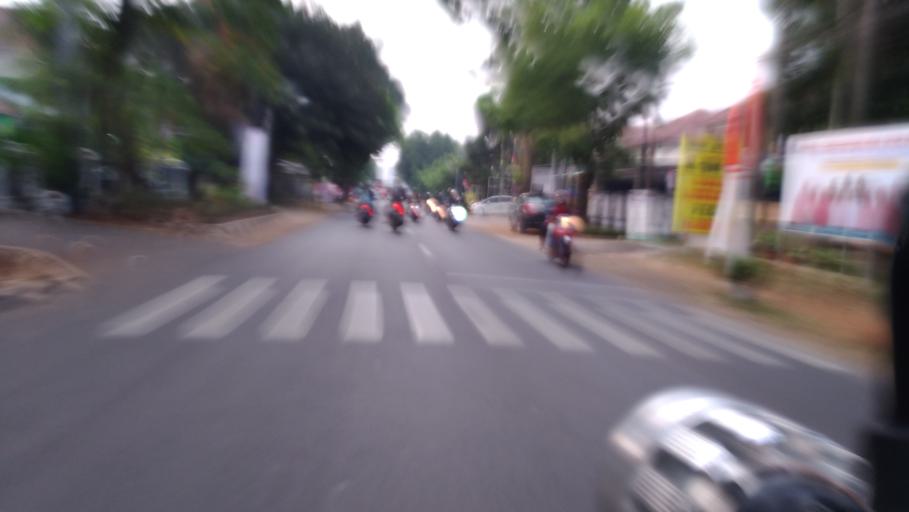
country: ID
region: West Java
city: Cileungsir
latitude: -6.3541
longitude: 106.8886
